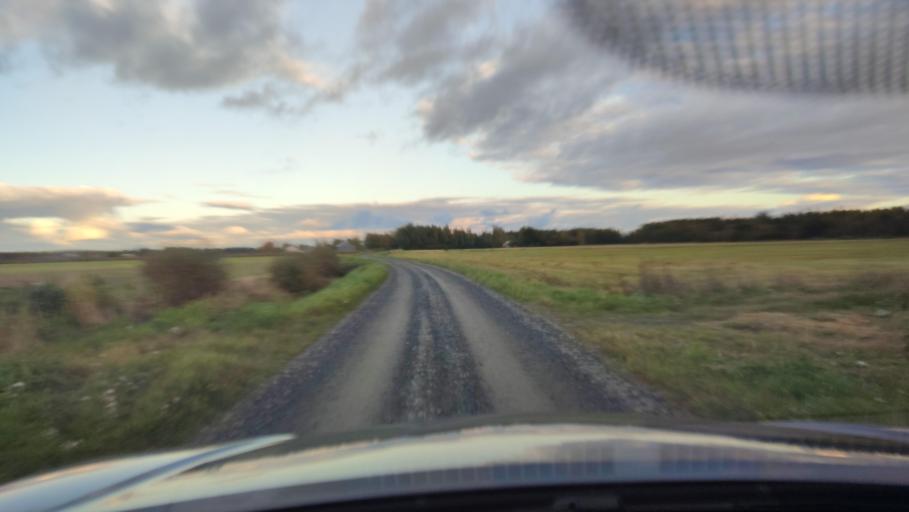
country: FI
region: Ostrobothnia
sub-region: Sydosterbotten
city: Kristinestad
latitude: 62.2502
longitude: 21.4688
